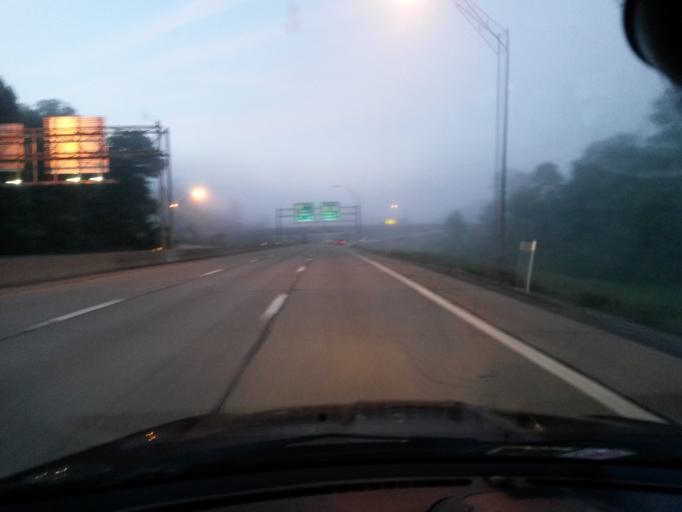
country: US
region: West Virginia
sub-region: Raleigh County
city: MacArthur
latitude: 37.7623
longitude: -81.2121
